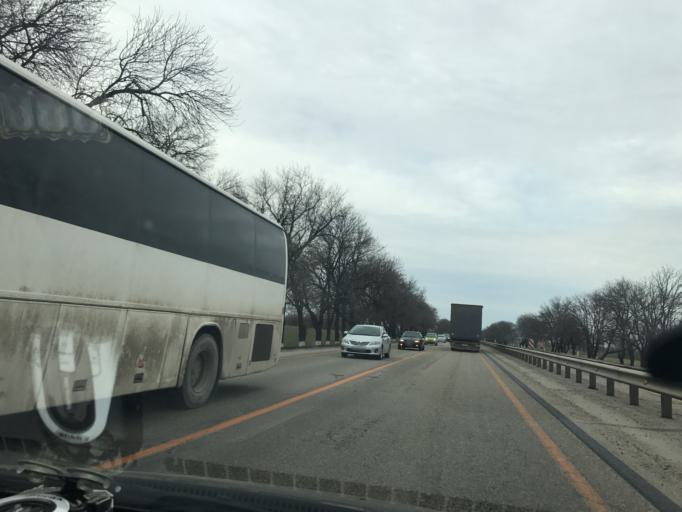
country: RU
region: Krasnodarskiy
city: Armavir
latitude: 44.9534
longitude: 41.0803
